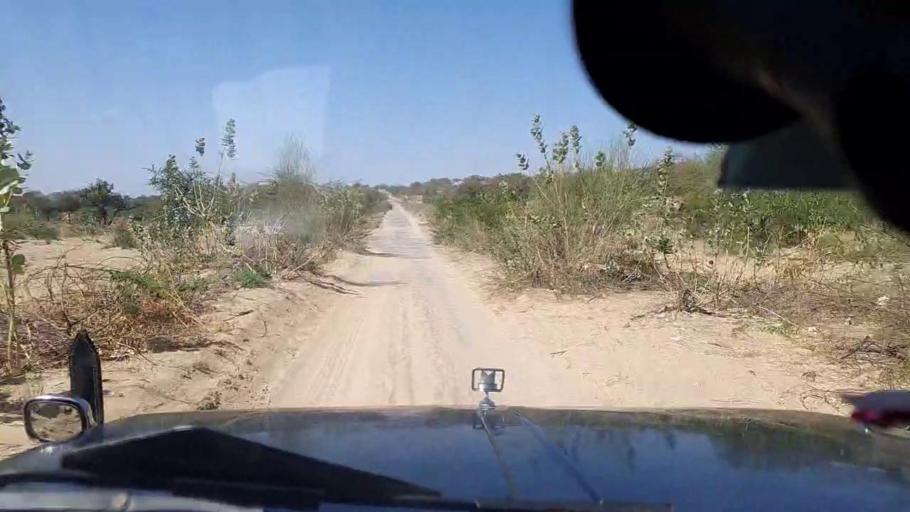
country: PK
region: Sindh
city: Mithi
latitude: 24.6118
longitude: 69.7050
